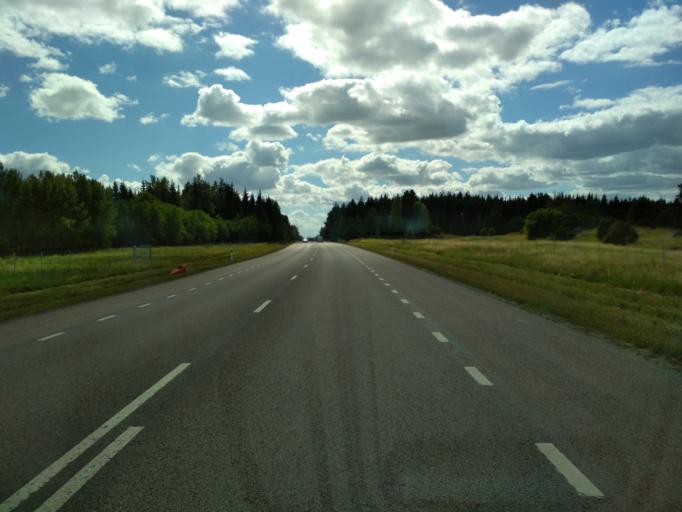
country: SE
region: Uppsala
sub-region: Uppsala Kommun
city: Uppsala
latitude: 59.8301
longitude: 17.5063
